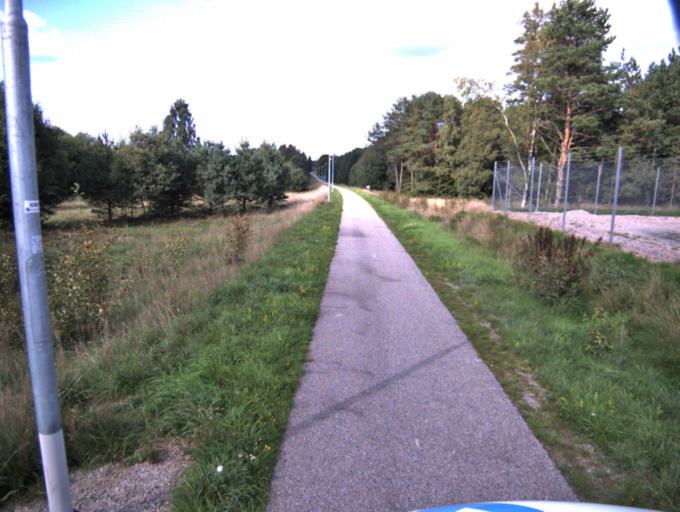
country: SE
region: Vaestra Goetaland
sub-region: Ulricehamns Kommun
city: Ulricehamn
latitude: 57.8638
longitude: 13.4294
